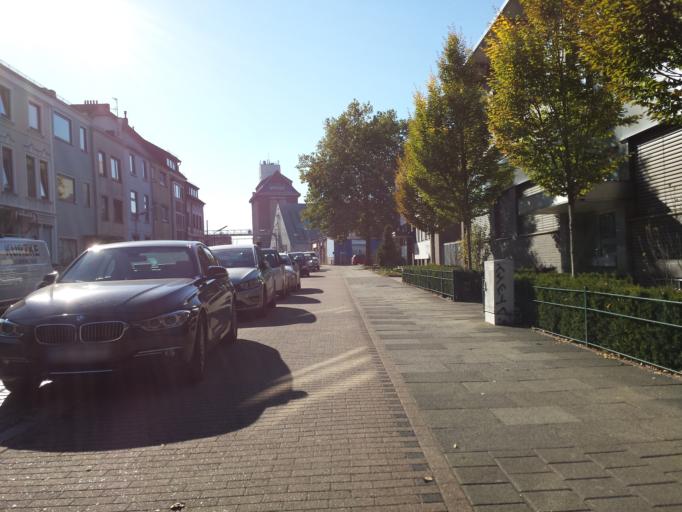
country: DE
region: Bremen
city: Bremen
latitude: 53.1020
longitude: 8.7753
